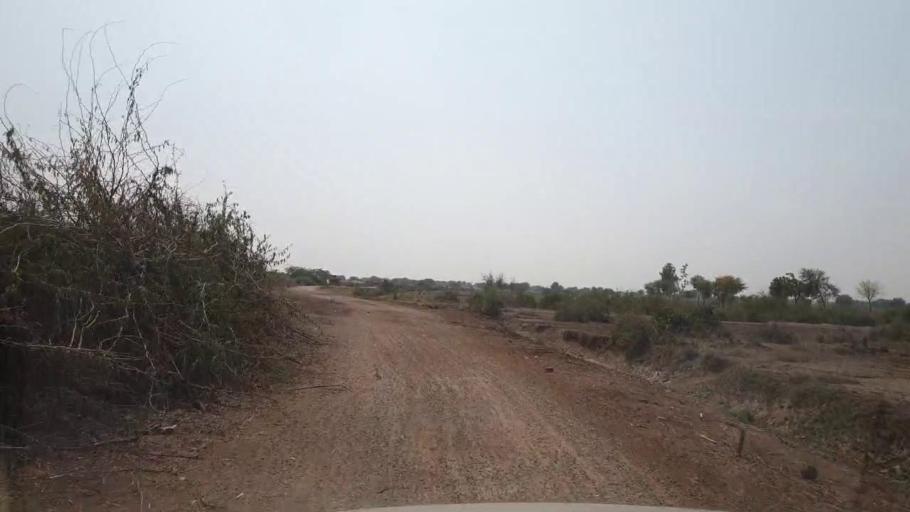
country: PK
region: Sindh
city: Dhoro Naro
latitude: 25.4887
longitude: 69.6452
